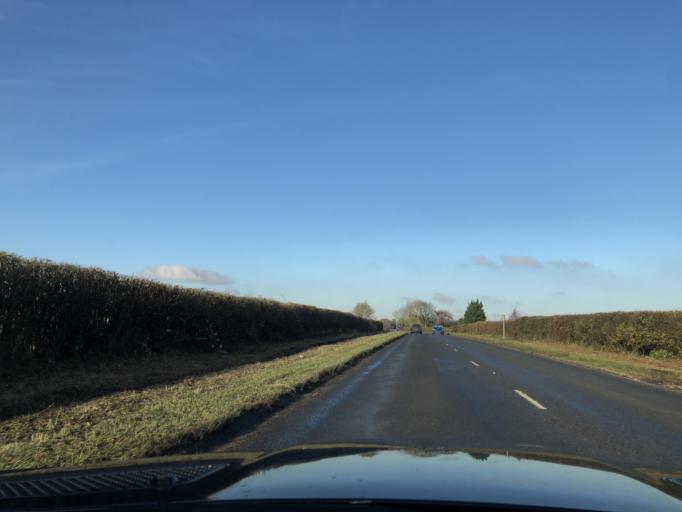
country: GB
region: England
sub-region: Buckinghamshire
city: High Wycombe
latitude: 51.6035
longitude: -0.7699
